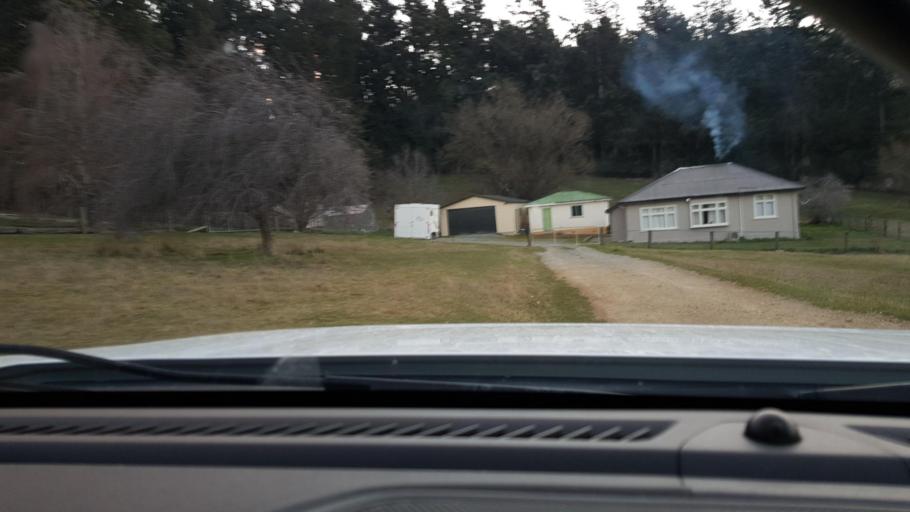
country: NZ
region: Otago
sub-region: Queenstown-Lakes District
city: Wanaka
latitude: -44.4828
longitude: 169.8344
